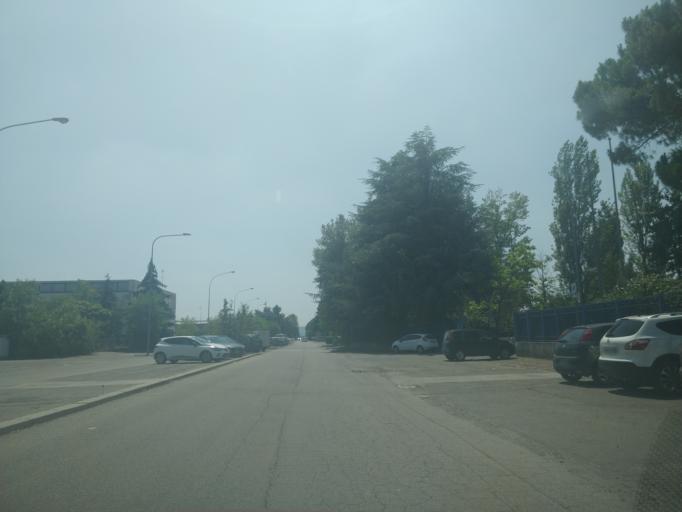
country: IT
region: Emilia-Romagna
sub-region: Provincia di Bologna
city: Progresso
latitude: 44.5620
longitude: 11.3715
